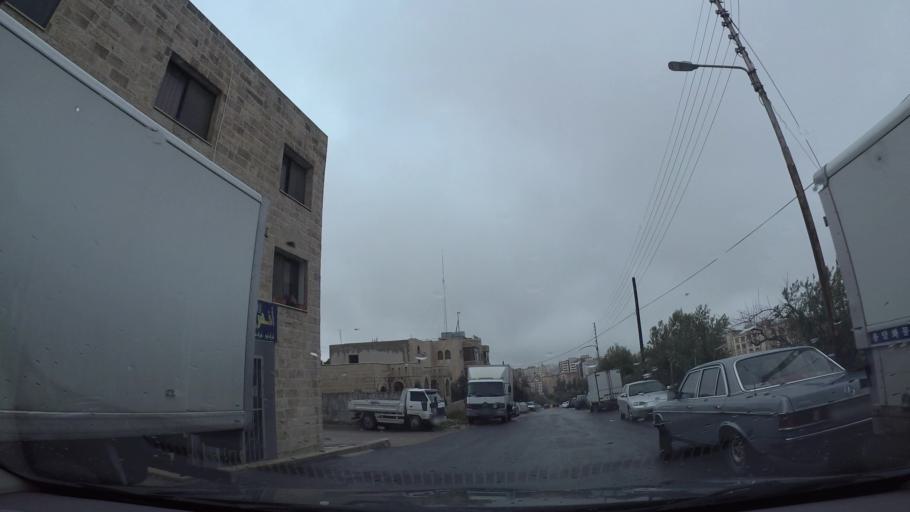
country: JO
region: Amman
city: Al Jubayhah
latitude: 32.0277
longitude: 35.8630
